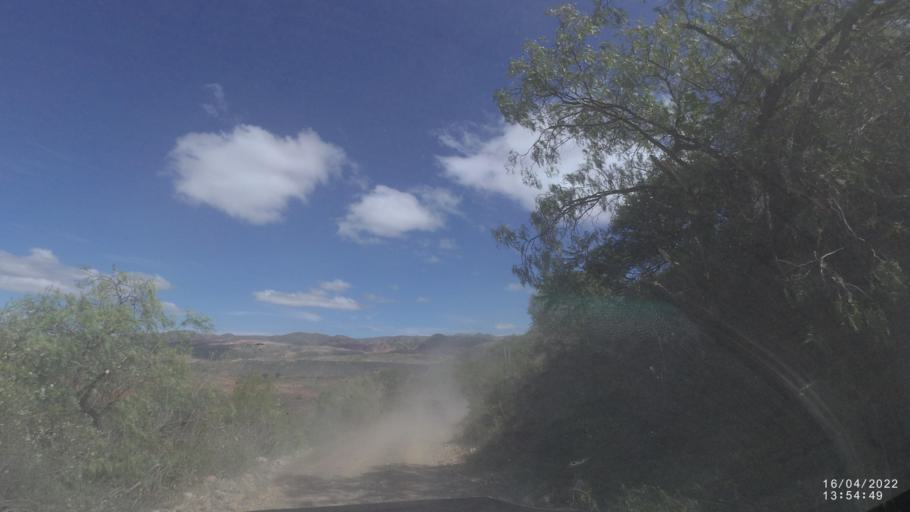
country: BO
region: Cochabamba
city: Mizque
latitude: -18.0264
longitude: -65.5634
